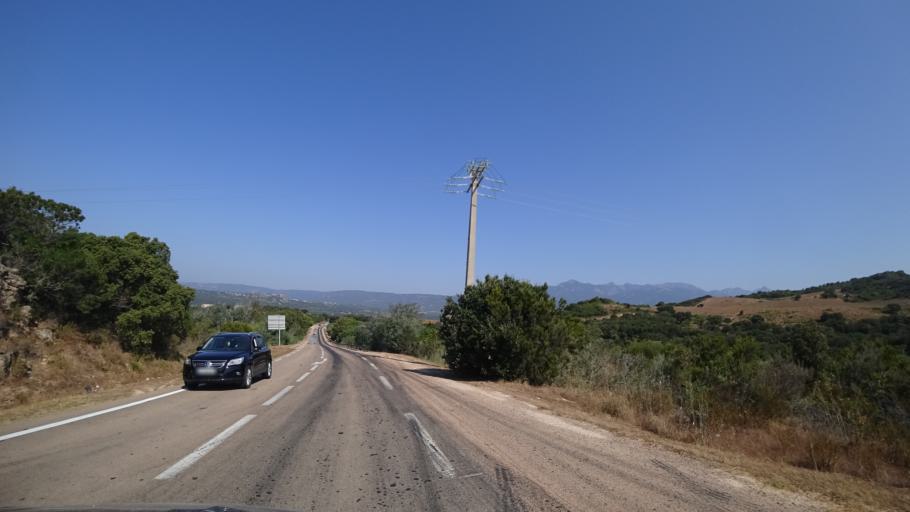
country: FR
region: Corsica
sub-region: Departement de la Corse-du-Sud
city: Bonifacio
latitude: 41.4708
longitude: 9.0953
